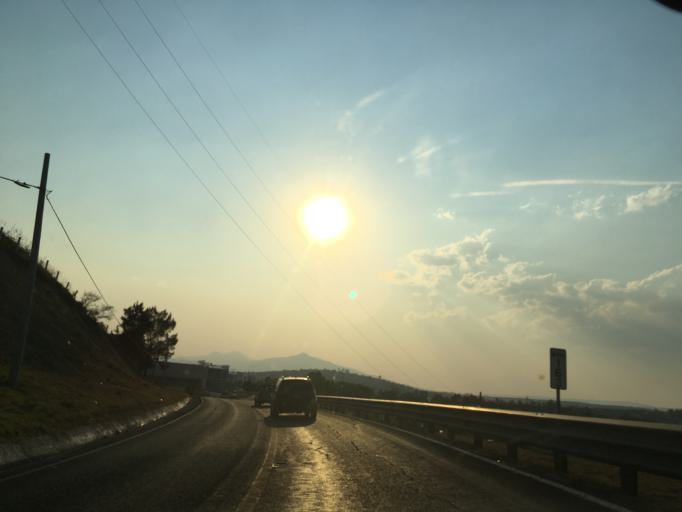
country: MX
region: Michoacan
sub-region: Morelia
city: La Aldea
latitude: 19.7339
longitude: -101.1233
